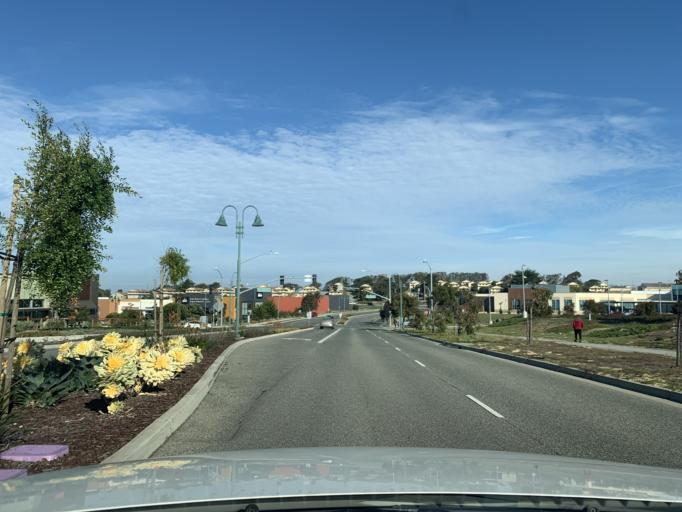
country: US
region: California
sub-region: Monterey County
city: Marina
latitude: 36.6654
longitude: -121.8092
